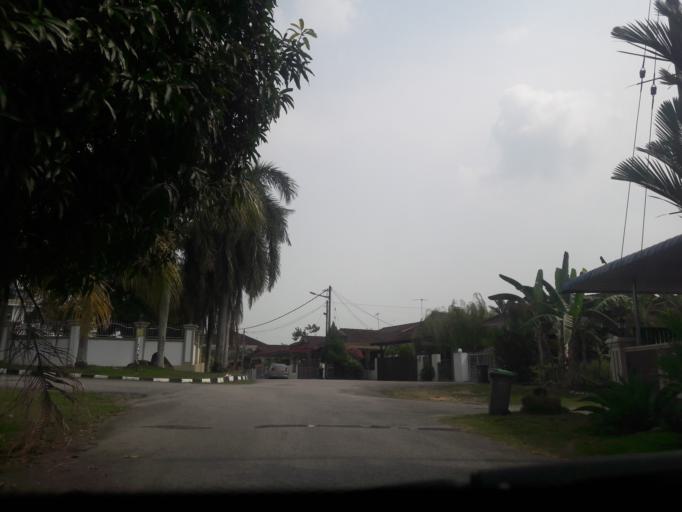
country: MY
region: Kedah
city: Kulim
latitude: 5.3656
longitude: 100.5387
